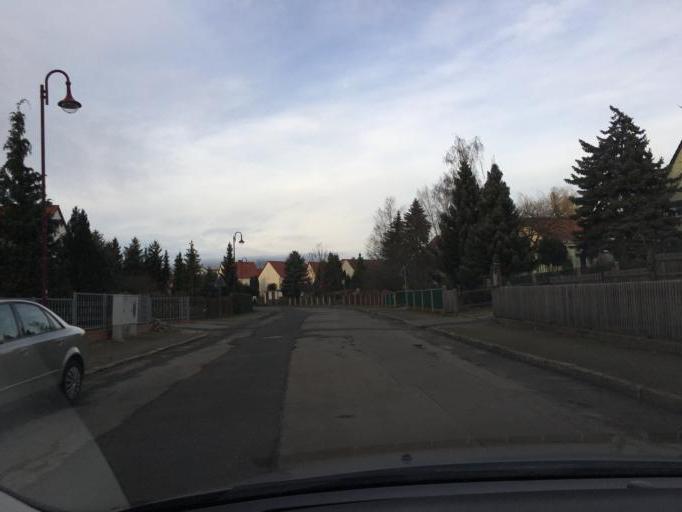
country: DE
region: Saxony
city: Grossposna
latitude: 51.2475
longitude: 12.4708
